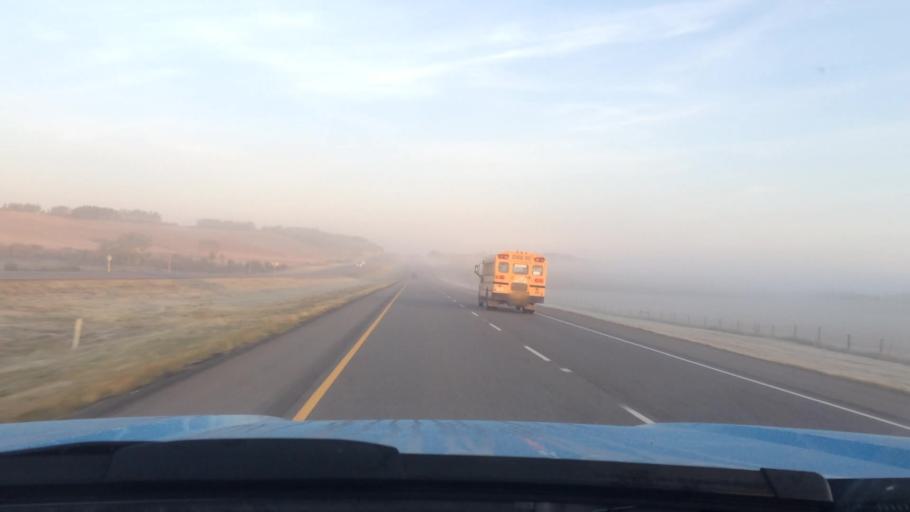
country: CA
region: Alberta
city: Cochrane
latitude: 51.0930
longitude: -114.5826
